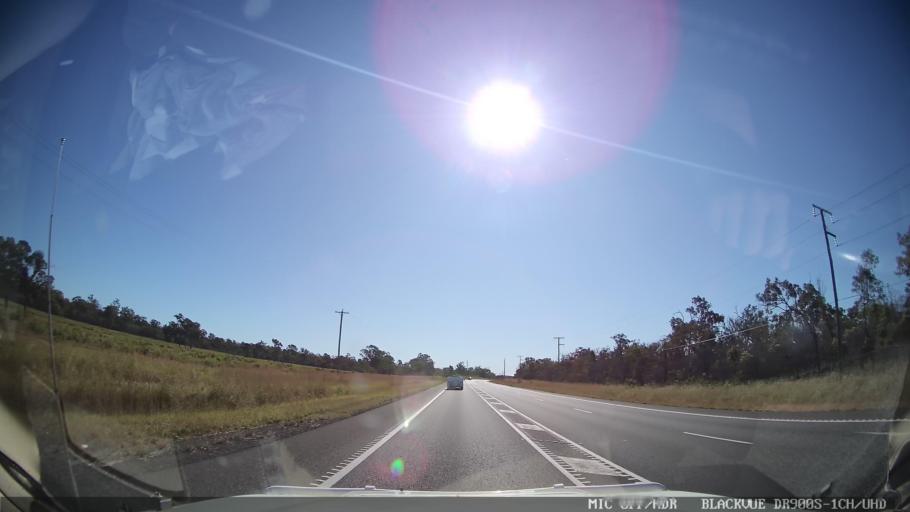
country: AU
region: Queensland
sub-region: Bundaberg
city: Childers
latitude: -25.2746
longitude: 152.3813
